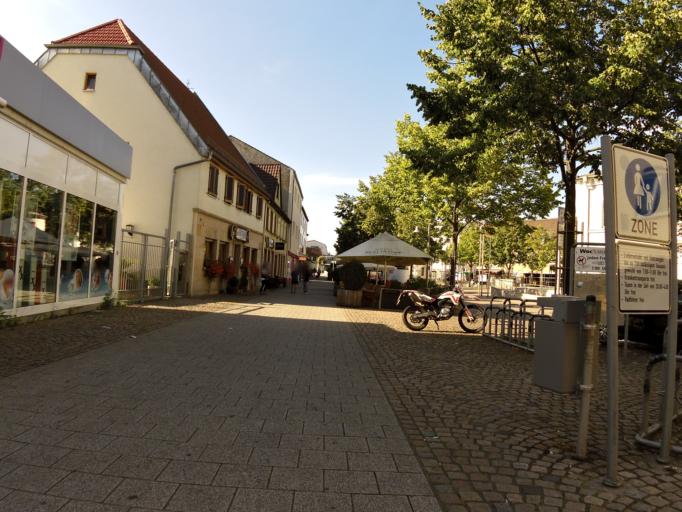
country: DE
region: Rheinland-Pfalz
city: Gartenstadt
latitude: 49.4920
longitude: 8.3762
